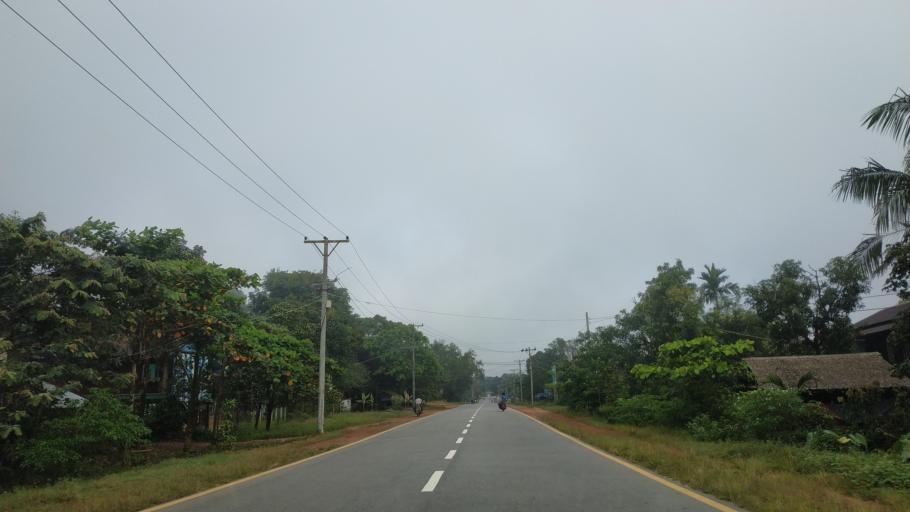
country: MM
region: Tanintharyi
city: Dawei
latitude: 14.1520
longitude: 98.2055
